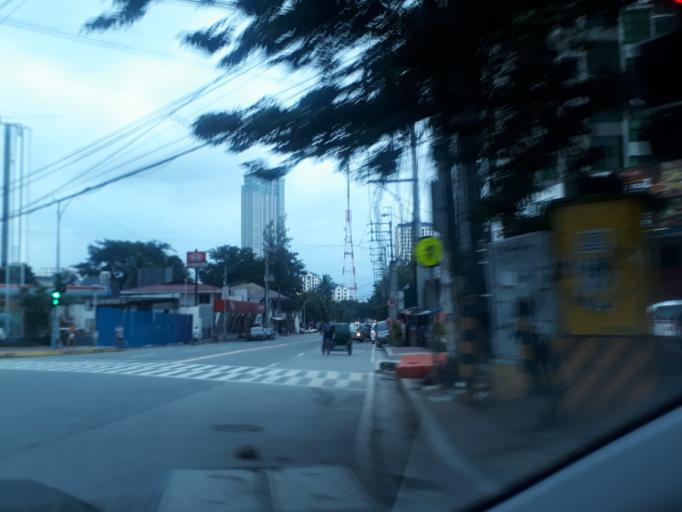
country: PH
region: Metro Manila
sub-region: Quezon City
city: Quezon City
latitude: 14.6335
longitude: 121.0418
